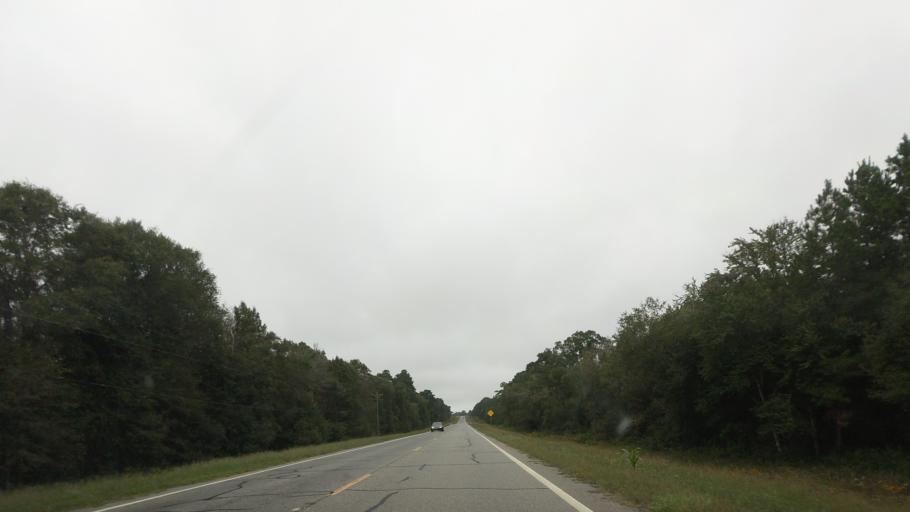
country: US
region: Georgia
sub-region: Irwin County
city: Ocilla
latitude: 31.4971
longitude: -83.2386
